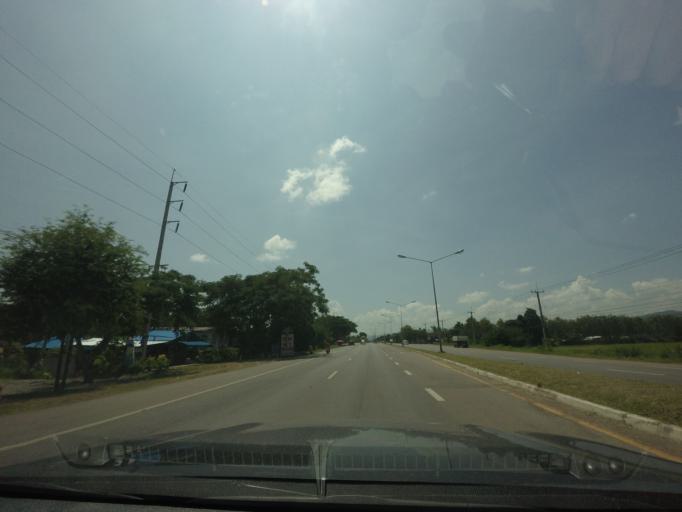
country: TH
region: Phetchabun
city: Lom Sak
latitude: 16.7134
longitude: 101.1796
